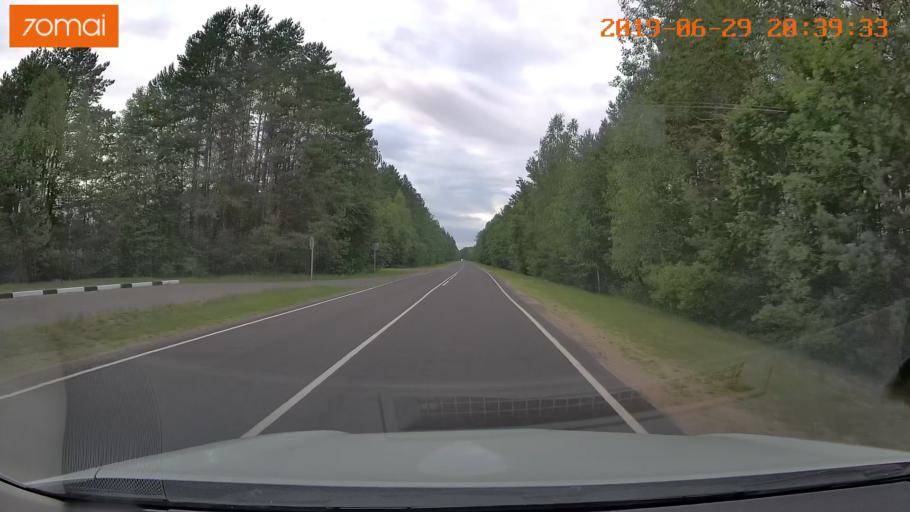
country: BY
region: Brest
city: Hantsavichy
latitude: 52.5639
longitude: 26.3619
